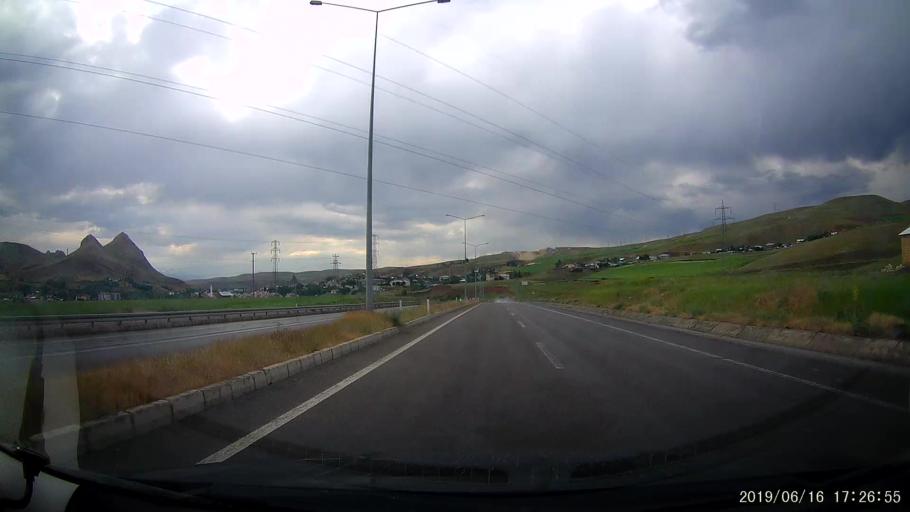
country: TR
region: Erzincan
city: Tercan
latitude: 39.7728
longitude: 40.4029
